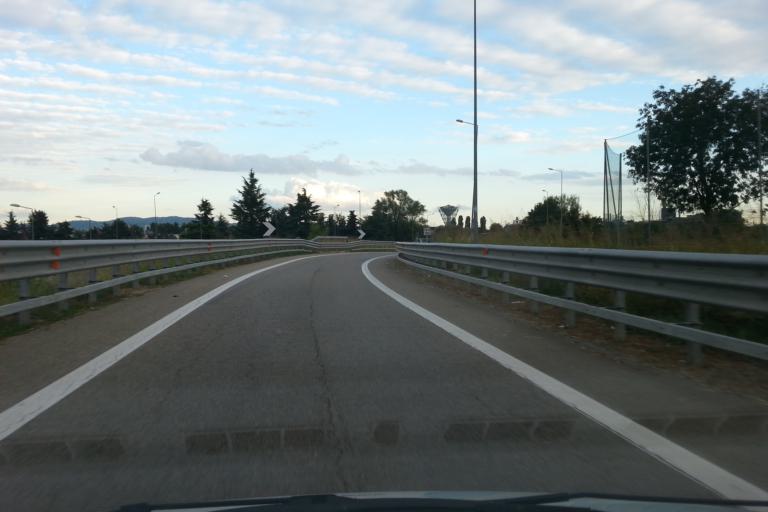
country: IT
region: Piedmont
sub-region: Provincia di Torino
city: Savonera
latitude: 45.1066
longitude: 7.5971
